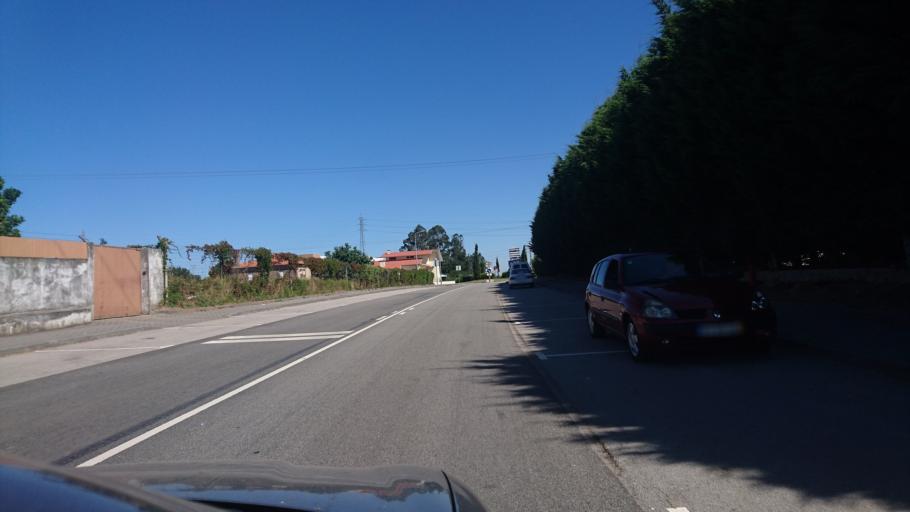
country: PT
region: Aveiro
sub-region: Santa Maria da Feira
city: Rio Meao
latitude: 40.9576
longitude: -8.5889
